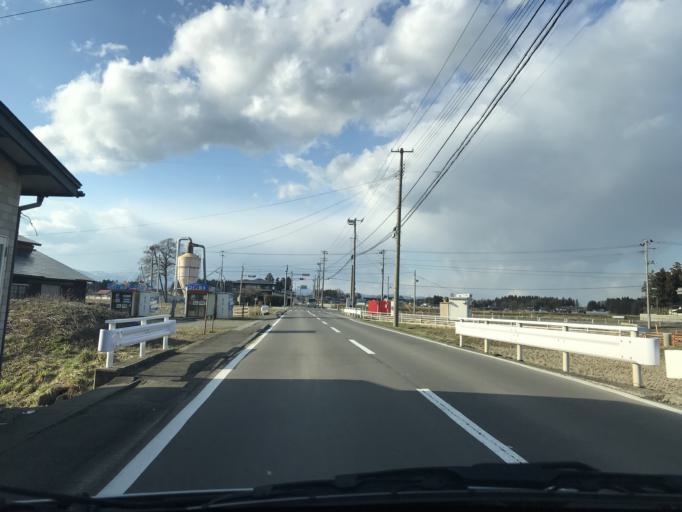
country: JP
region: Iwate
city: Kitakami
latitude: 39.3102
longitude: 141.0703
